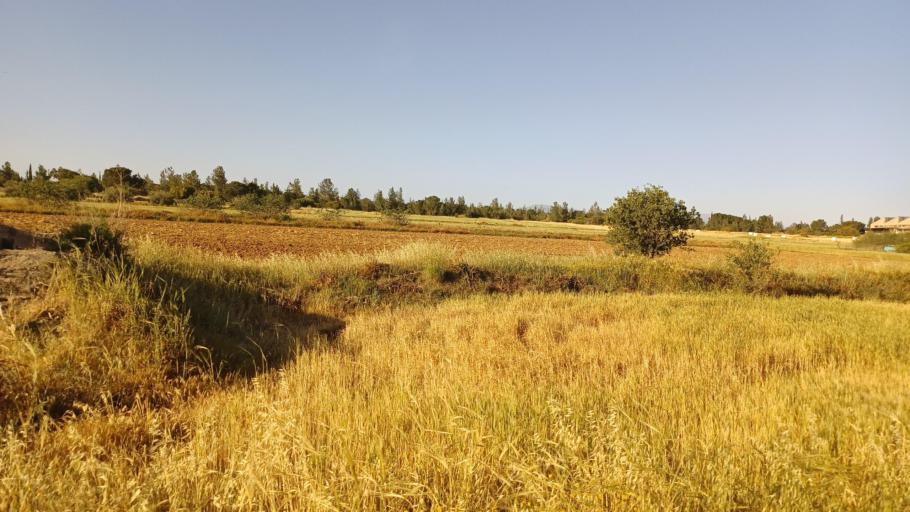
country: CY
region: Lefkosia
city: Kokkinotrimithia
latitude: 35.1498
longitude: 33.1756
